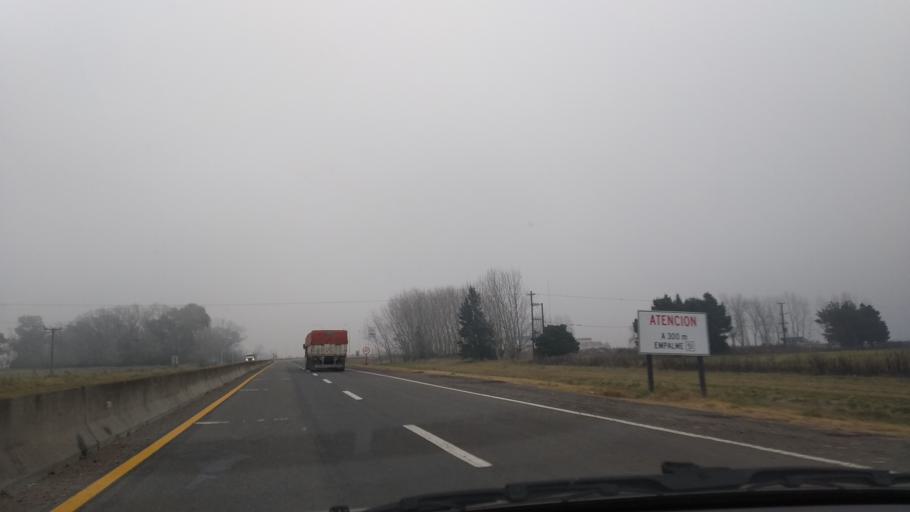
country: AR
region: Buenos Aires
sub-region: Partido de Azul
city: Azul
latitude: -36.8478
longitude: -59.9554
